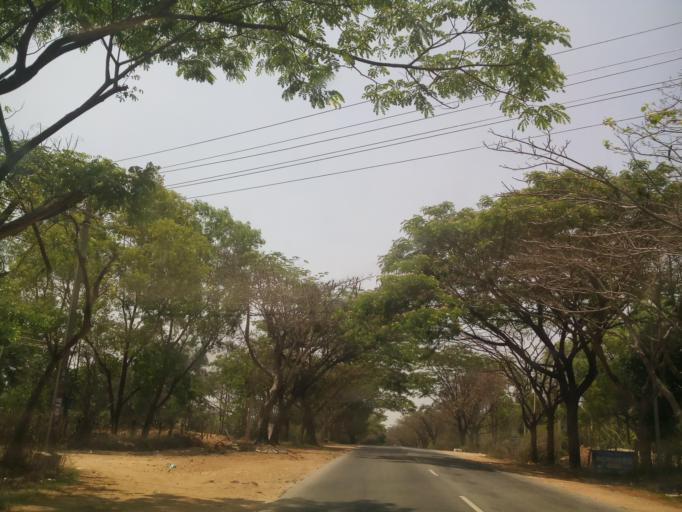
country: IN
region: Karnataka
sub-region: Hassan
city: Hassan
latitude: 12.9844
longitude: 76.0426
